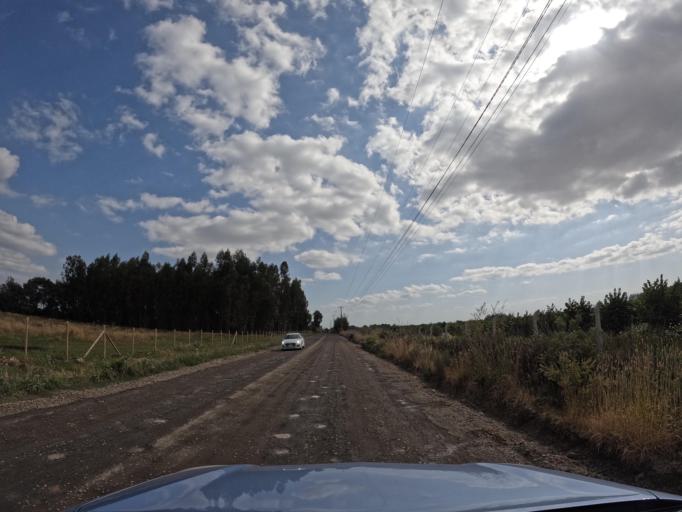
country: CL
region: Maule
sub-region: Provincia de Curico
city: Molina
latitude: -35.1662
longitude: -71.2900
